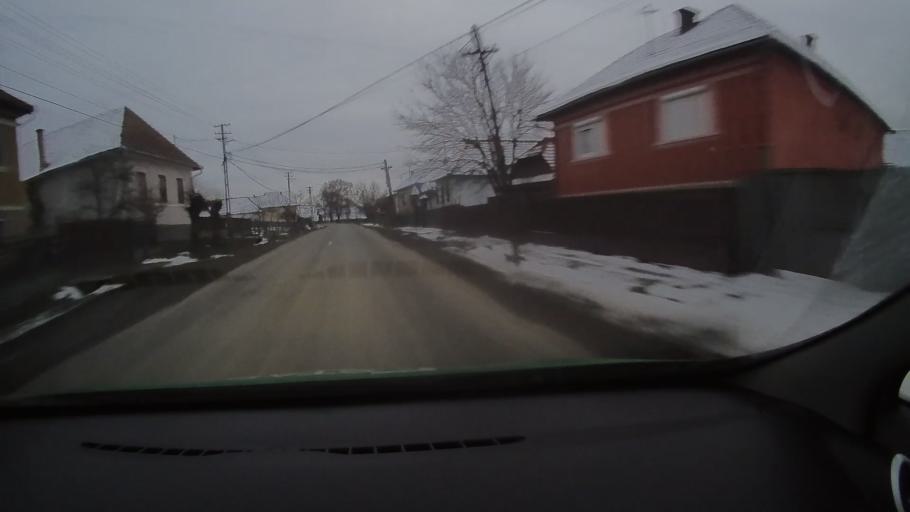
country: RO
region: Harghita
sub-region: Comuna Darjiu
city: Darjiu
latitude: 46.2116
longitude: 25.2400
